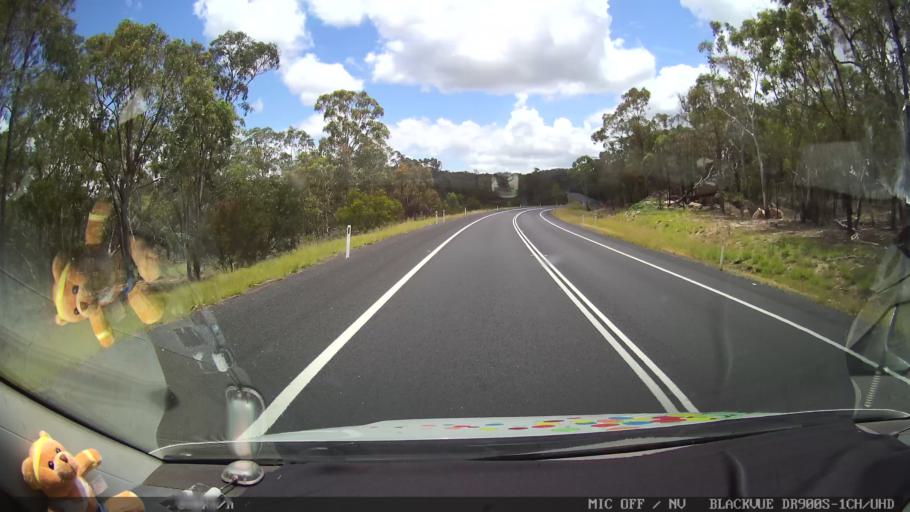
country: AU
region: New South Wales
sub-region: Glen Innes Severn
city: Glen Innes
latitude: -29.3571
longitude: 151.8977
